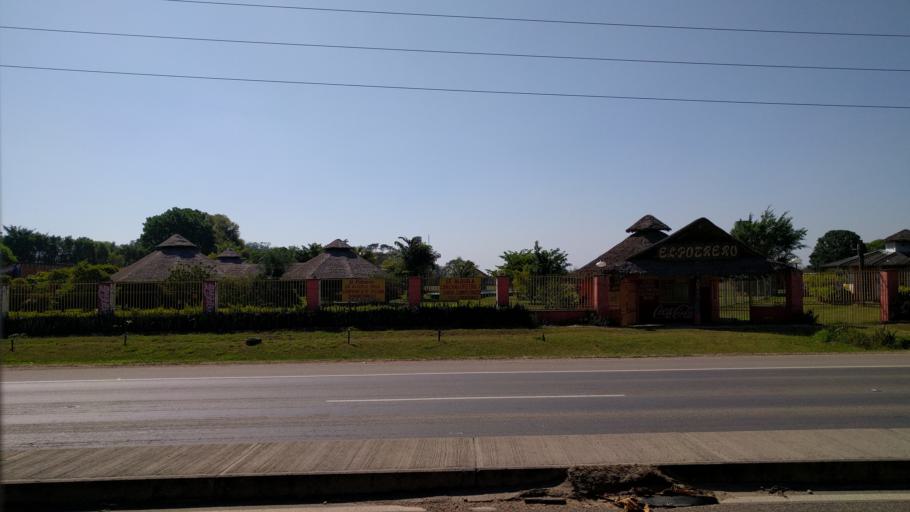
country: BO
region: Santa Cruz
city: Cotoca
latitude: -17.7652
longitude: -63.0392
